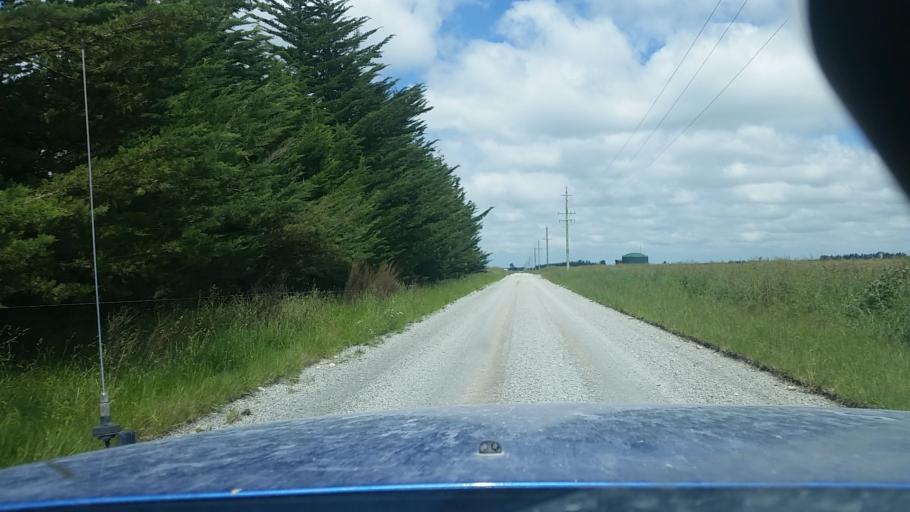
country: NZ
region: Canterbury
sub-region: Ashburton District
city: Tinwald
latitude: -43.8566
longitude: 171.3747
